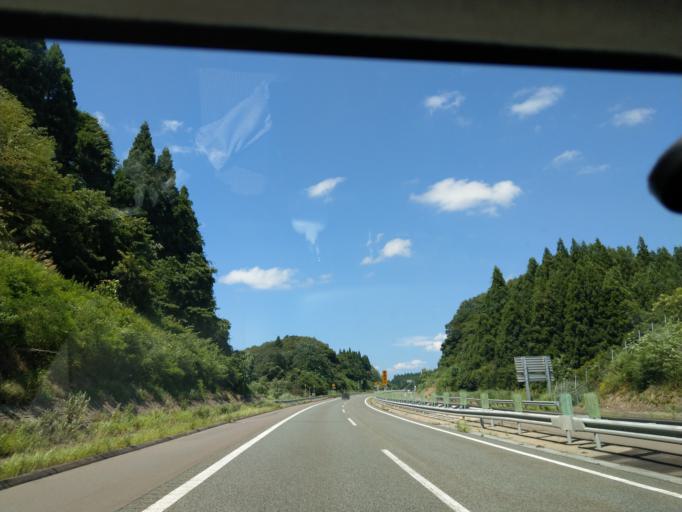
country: JP
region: Akita
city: Akita
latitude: 39.6632
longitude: 140.1890
